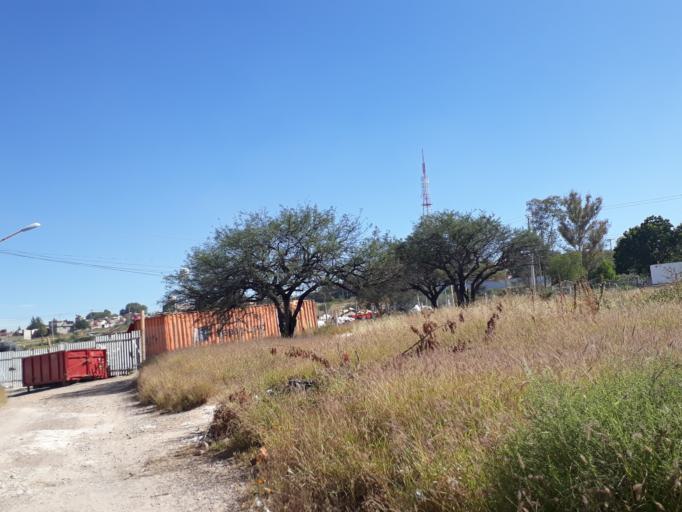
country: MX
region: Aguascalientes
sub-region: Aguascalientes
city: Villa Licenciado Jesus Teran (Calvillito)
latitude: 21.8606
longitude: -102.2308
